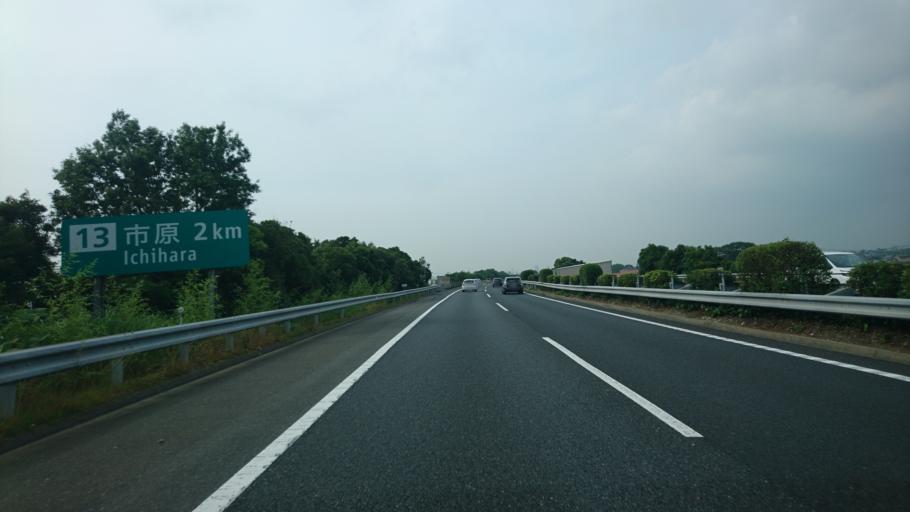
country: JP
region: Chiba
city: Ichihara
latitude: 35.4802
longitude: 140.0810
